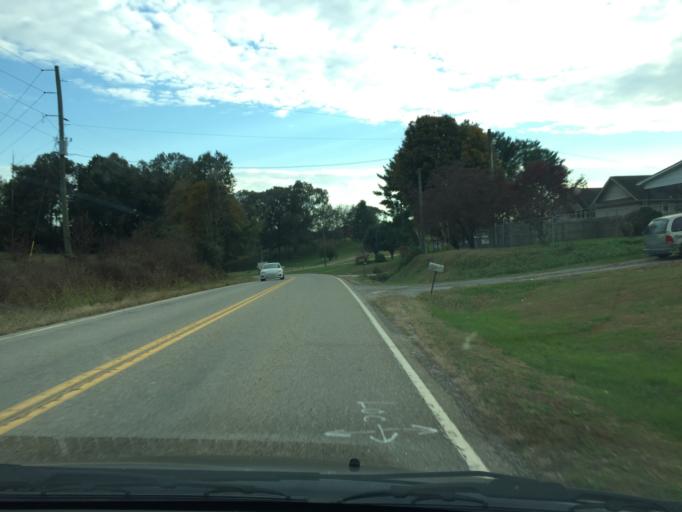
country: US
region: Tennessee
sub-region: Monroe County
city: Sweetwater
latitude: 35.6313
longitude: -84.5047
